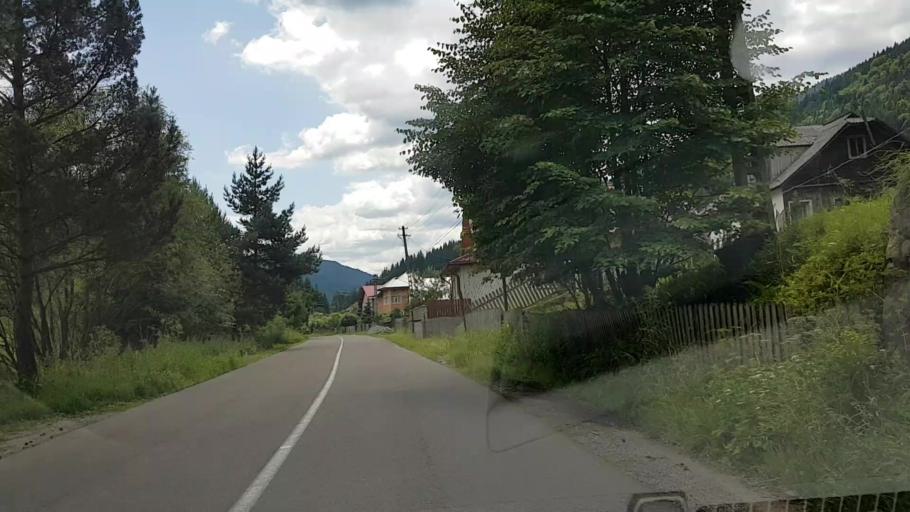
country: RO
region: Suceava
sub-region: Comuna Crucea
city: Crucea
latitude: 47.3452
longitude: 25.6079
